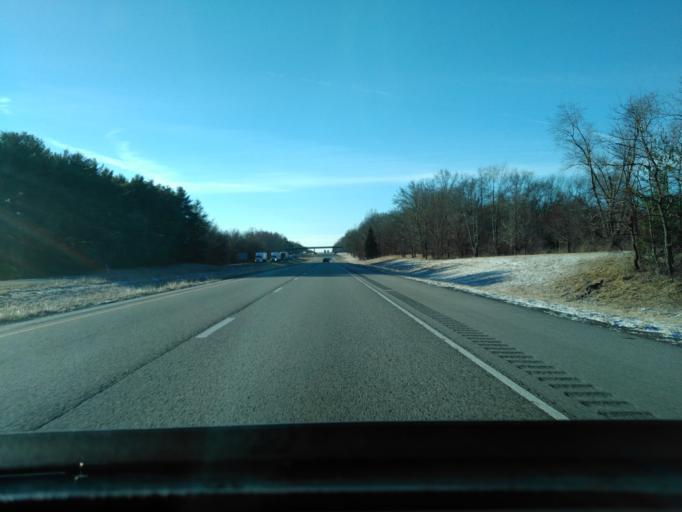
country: US
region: Illinois
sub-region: Franklin County
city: Benton
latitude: 37.9701
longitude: -88.9356
